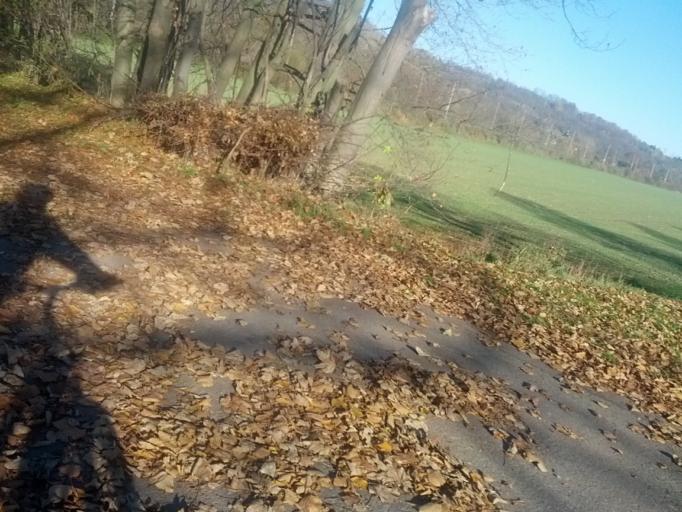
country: DE
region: Thuringia
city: Seebach
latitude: 50.9434
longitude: 10.4666
